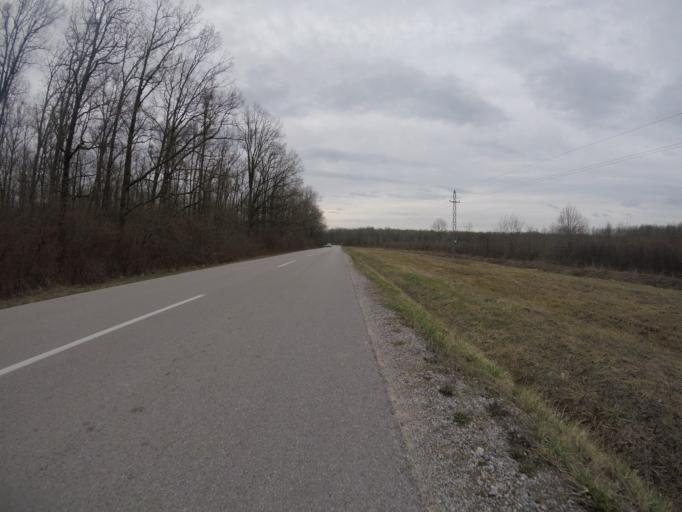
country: HR
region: Zagrebacka
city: Lukavec
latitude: 45.6860
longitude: 15.9802
